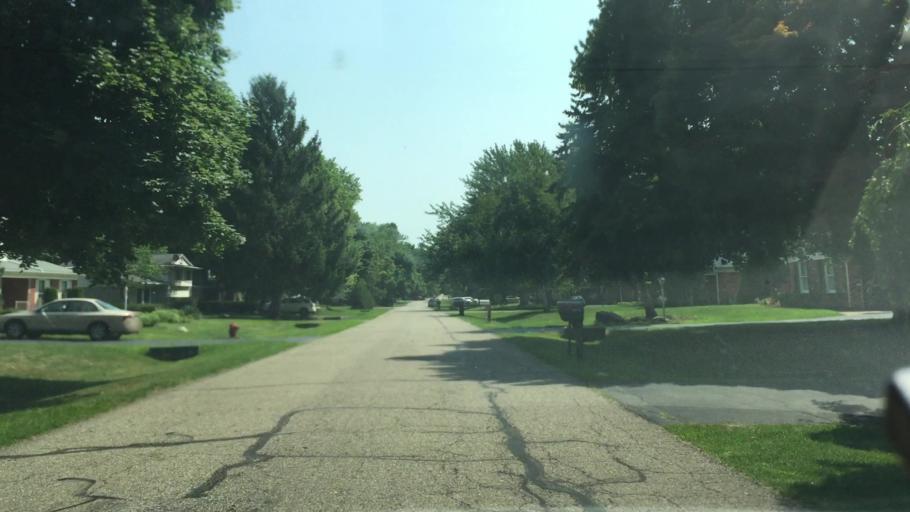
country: US
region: Michigan
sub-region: Oakland County
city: West Bloomfield Township
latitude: 42.5381
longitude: -83.3550
